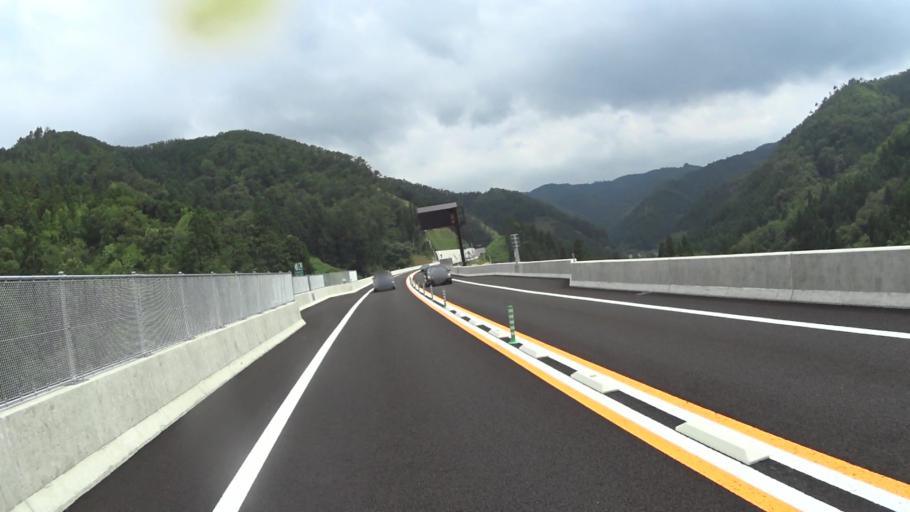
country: JP
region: Kyoto
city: Ayabe
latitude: 35.2651
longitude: 135.3455
